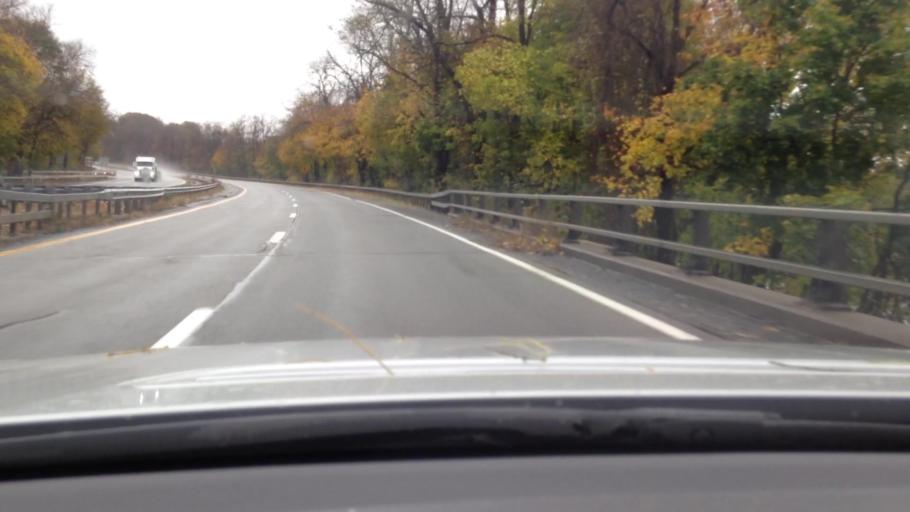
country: US
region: New York
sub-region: Westchester County
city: Buchanan
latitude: 41.2706
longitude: -73.9344
